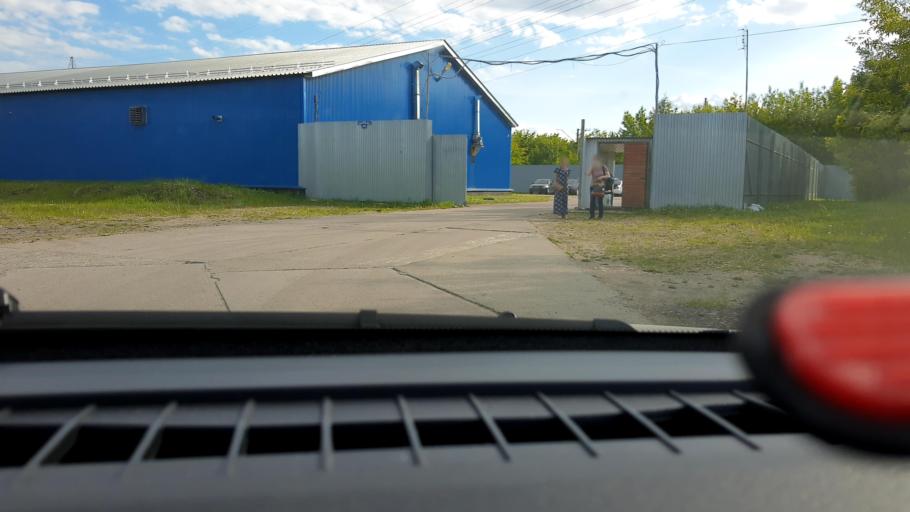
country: RU
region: Nizjnij Novgorod
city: Neklyudovo
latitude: 56.3482
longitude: 43.8822
